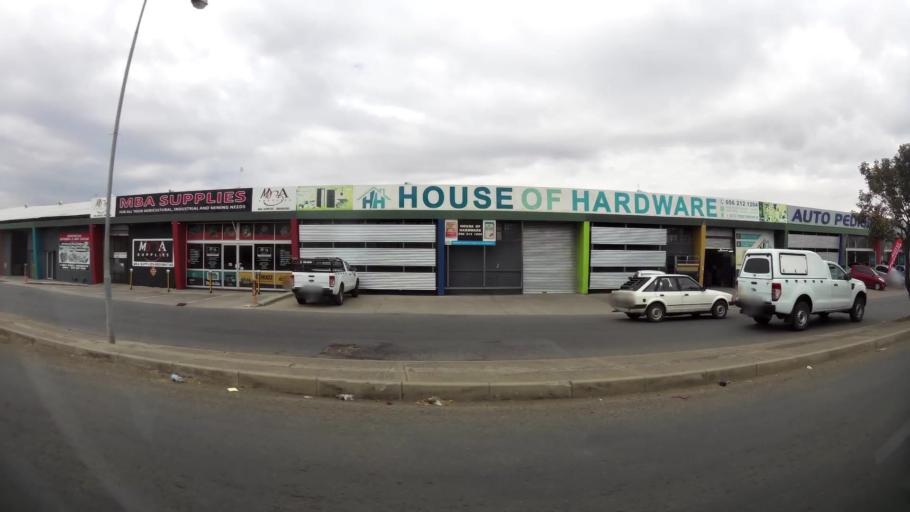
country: ZA
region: Orange Free State
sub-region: Fezile Dabi District Municipality
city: Kroonstad
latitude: -27.6634
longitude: 27.2296
